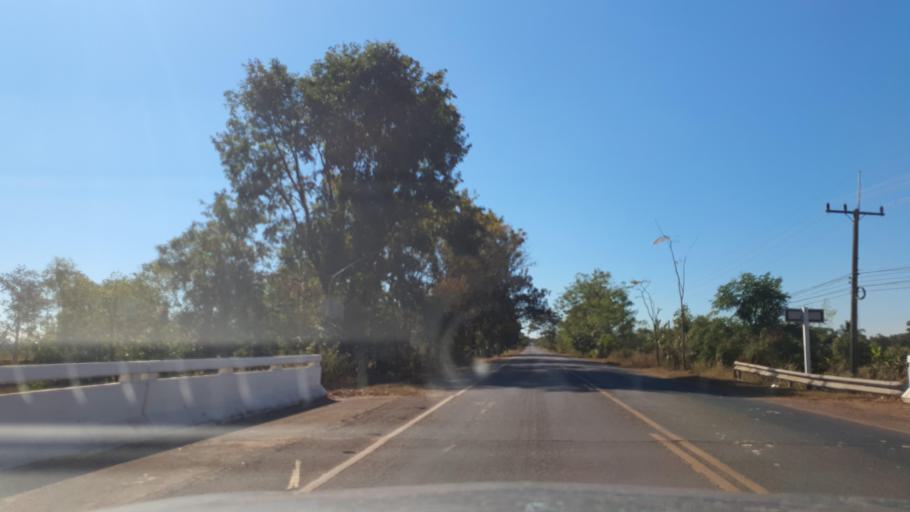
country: TH
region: Nakhon Phanom
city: Si Songkhram
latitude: 17.7490
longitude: 104.2862
